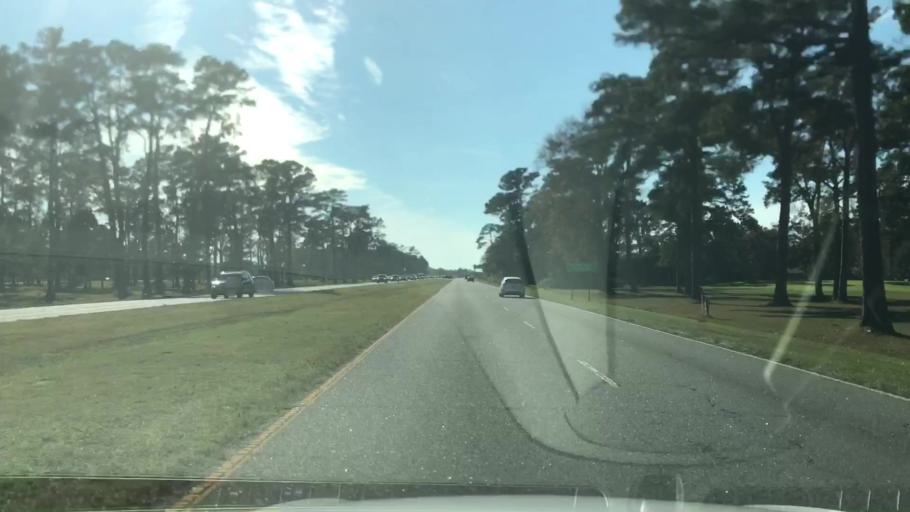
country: US
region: South Carolina
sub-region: Horry County
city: Myrtle Beach
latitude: 33.7269
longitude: -78.8719
